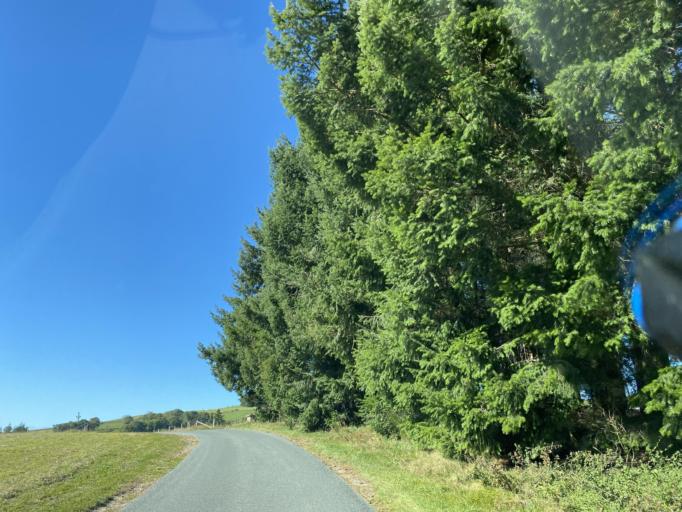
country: FR
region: Rhone-Alpes
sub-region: Departement de la Loire
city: Saint-Just-en-Chevalet
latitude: 45.9614
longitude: 3.8743
